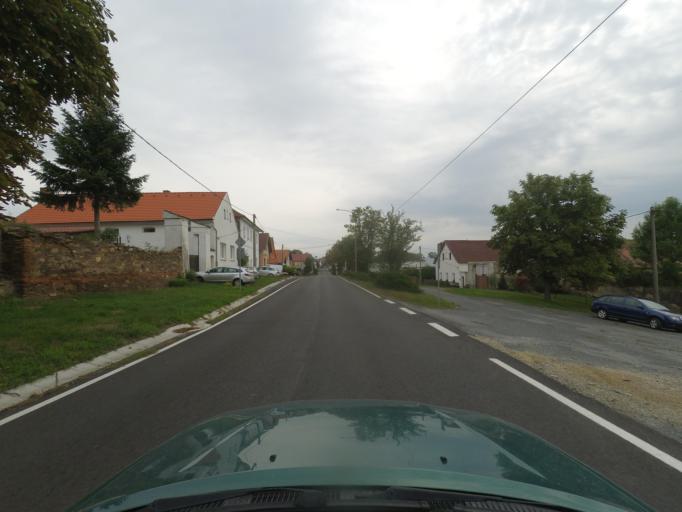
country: CZ
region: Plzensky
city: Meclov
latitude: 49.5366
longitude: 12.8873
